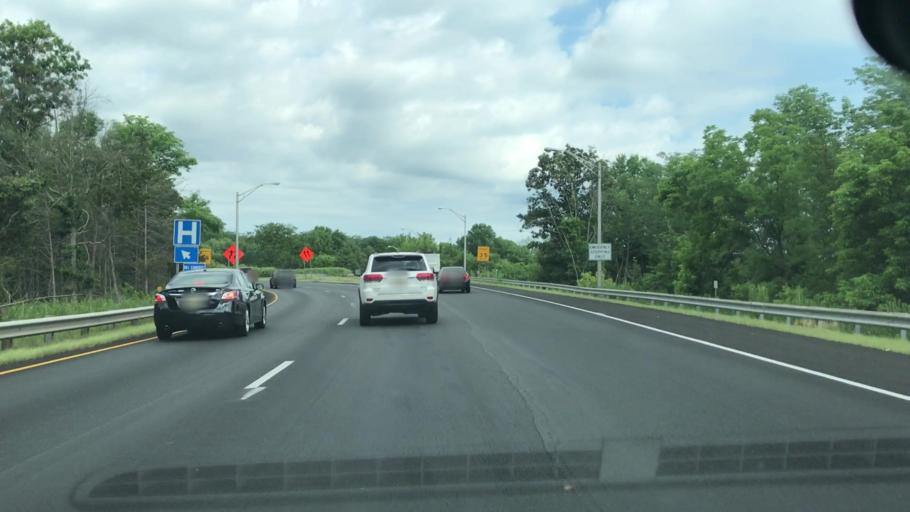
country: US
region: New Jersey
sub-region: Somerset County
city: Bedminster
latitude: 40.6442
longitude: -74.6429
